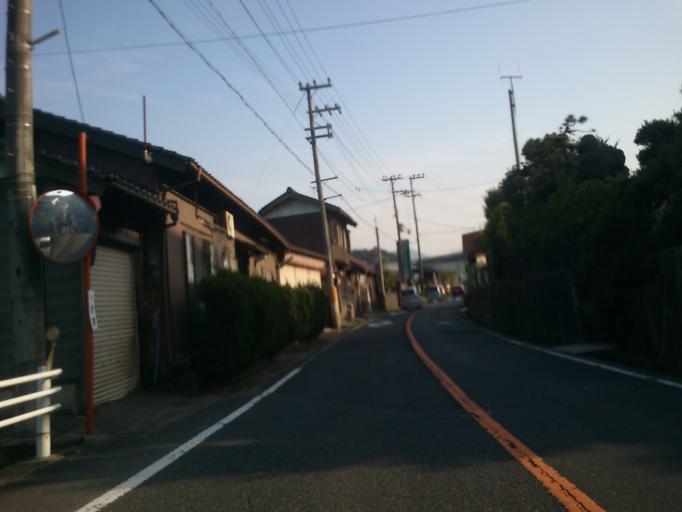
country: JP
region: Kyoto
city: Miyazu
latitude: 35.5554
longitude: 135.1391
